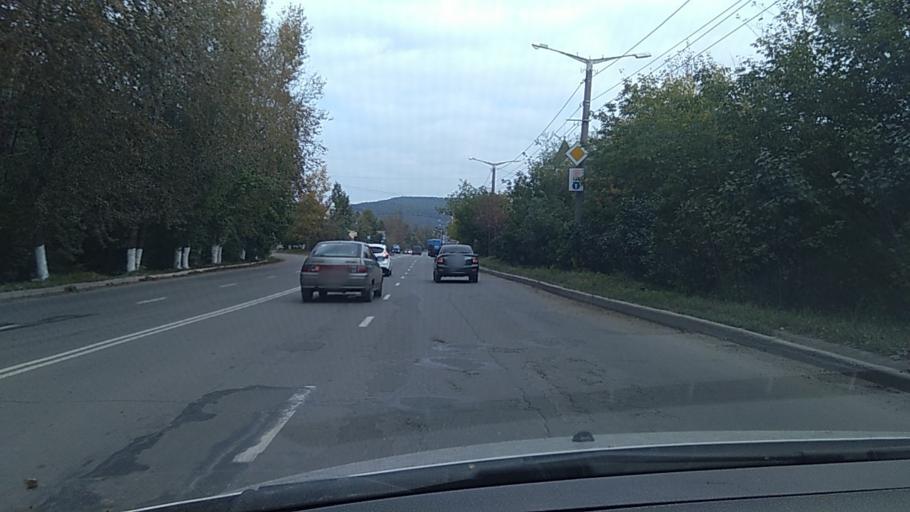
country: RU
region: Chelyabinsk
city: Zlatoust
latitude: 55.1524
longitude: 59.6787
